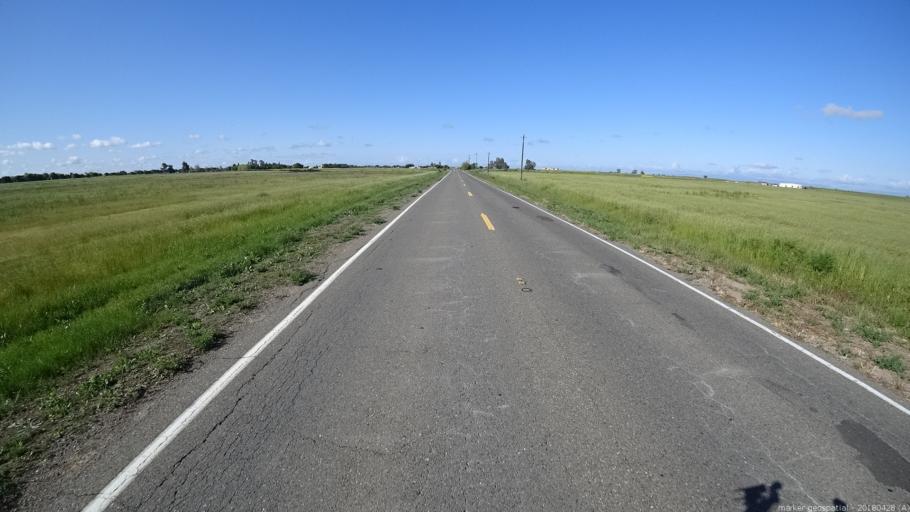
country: US
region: California
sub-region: Yolo County
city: West Sacramento
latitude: 38.5179
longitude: -121.5697
